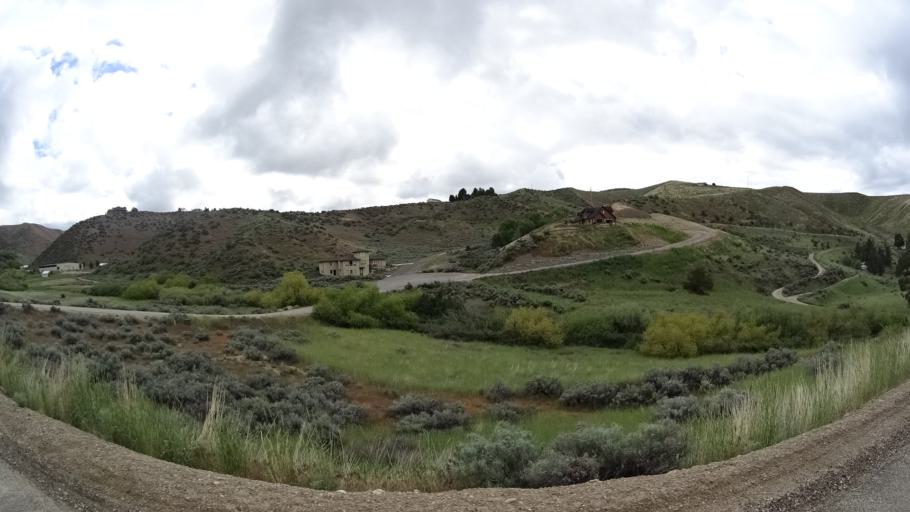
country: US
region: Idaho
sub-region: Ada County
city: Garden City
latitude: 43.6877
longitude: -116.2499
